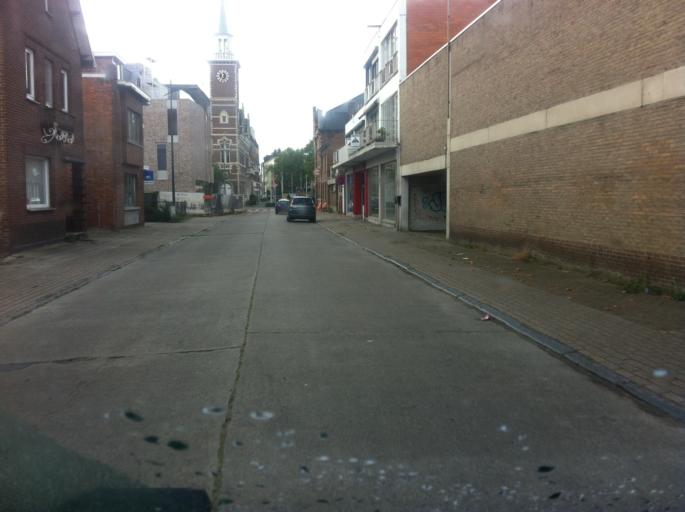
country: BE
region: Flanders
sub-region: Provincie Limburg
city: Maasmechelen
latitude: 50.9643
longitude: 5.6972
